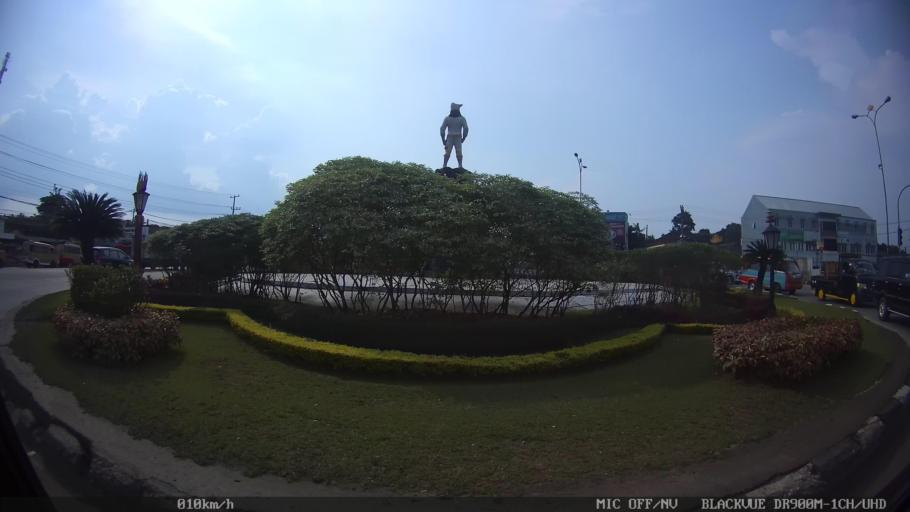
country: ID
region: Lampung
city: Kedaton
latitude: -5.3619
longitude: 105.2260
